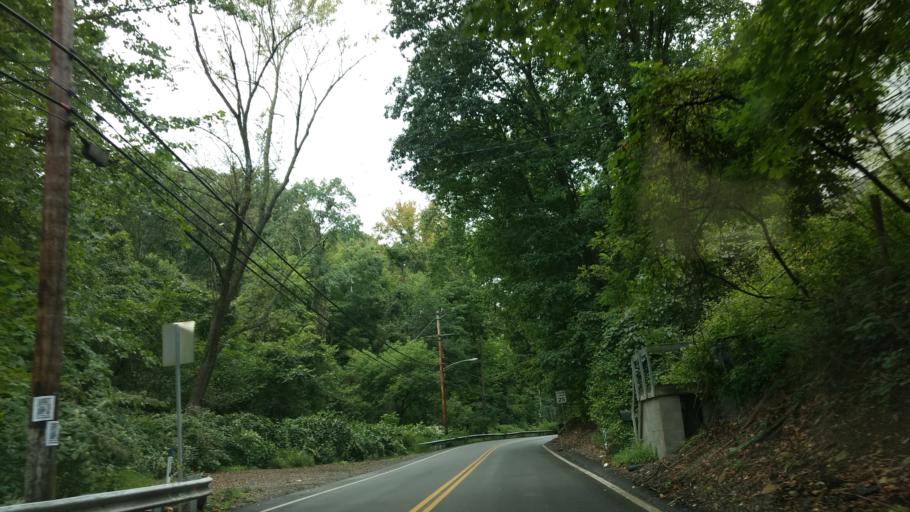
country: US
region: Pennsylvania
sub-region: Allegheny County
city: Bellevue
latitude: 40.4947
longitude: -80.0453
